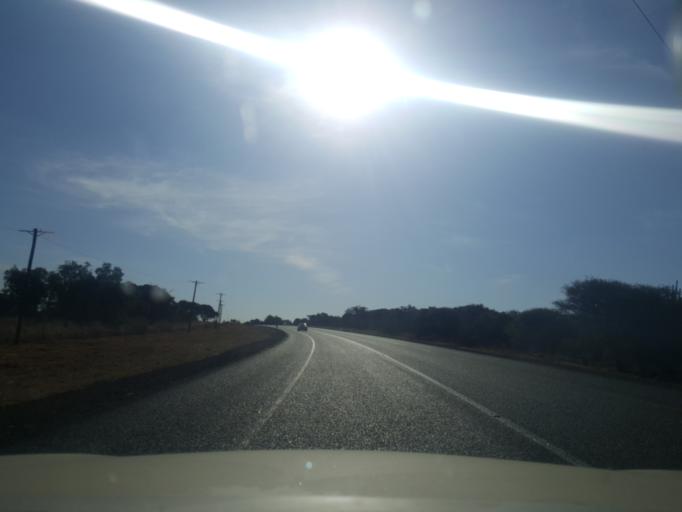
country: ZA
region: North-West
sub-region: Ngaka Modiri Molema District Municipality
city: Zeerust
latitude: -25.5406
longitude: 26.0425
